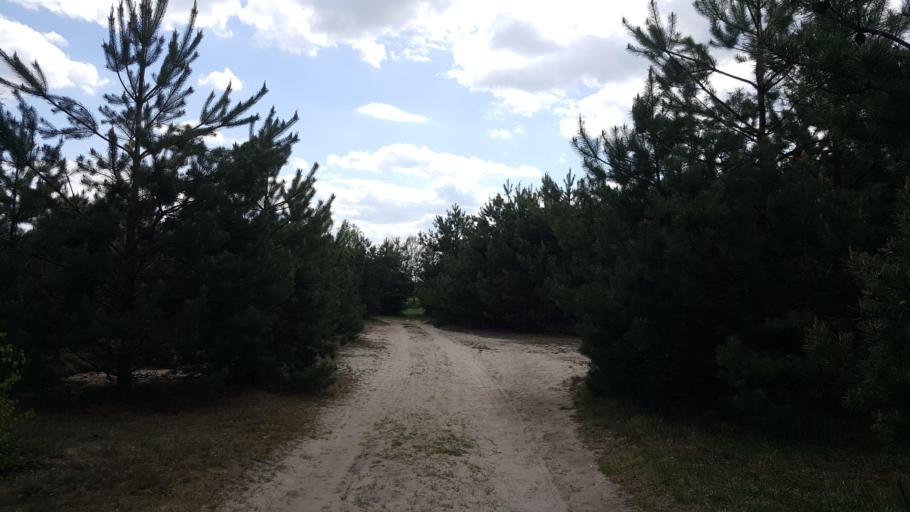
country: BY
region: Brest
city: Zhabinka
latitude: 52.4189
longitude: 24.1686
